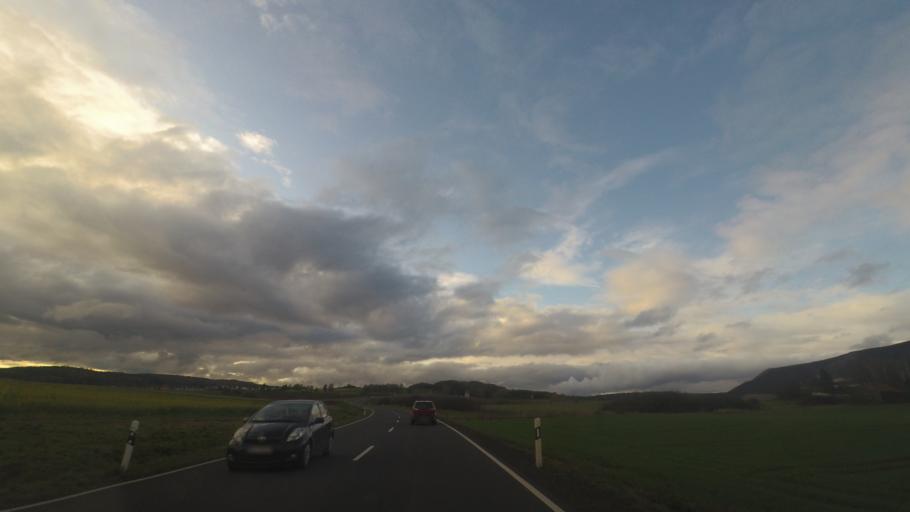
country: DE
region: Hesse
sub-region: Regierungsbezirk Kassel
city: Neuhof
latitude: 50.4515
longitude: 9.6014
